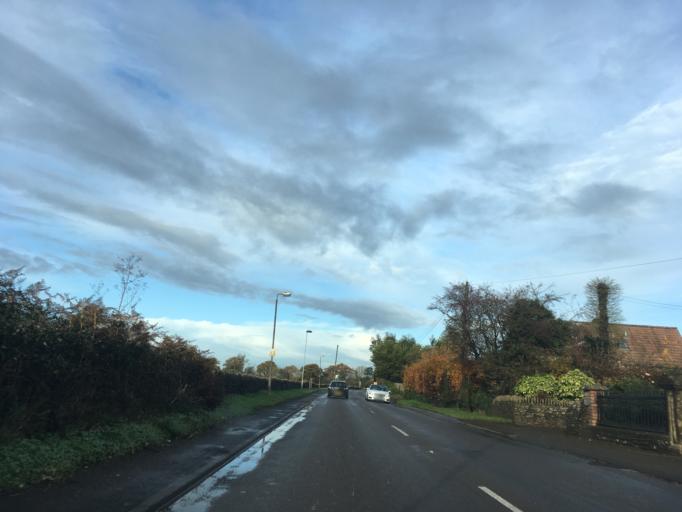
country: GB
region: England
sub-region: South Gloucestershire
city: Yate
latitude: 51.5592
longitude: -2.4525
